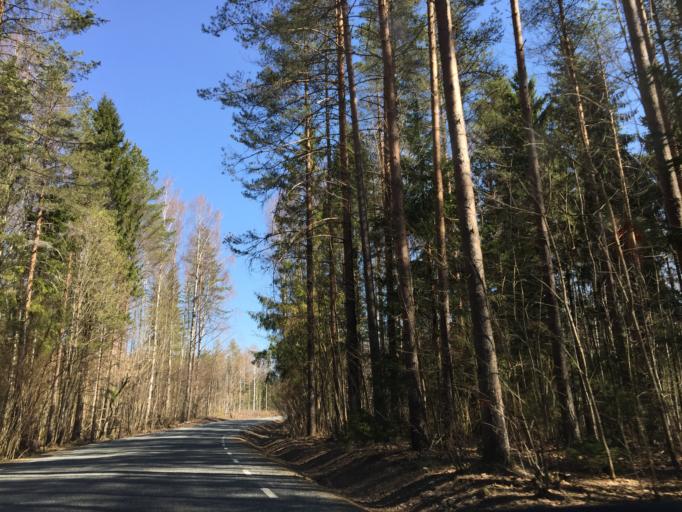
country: EE
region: Tartu
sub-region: Alatskivi vald
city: Kallaste
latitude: 58.5749
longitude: 26.9861
